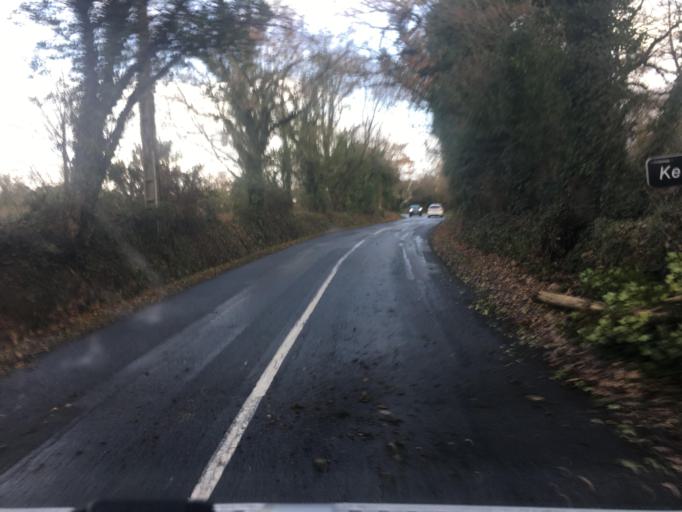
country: FR
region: Brittany
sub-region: Departement du Morbihan
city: Sarzeau
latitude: 47.5191
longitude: -2.7682
